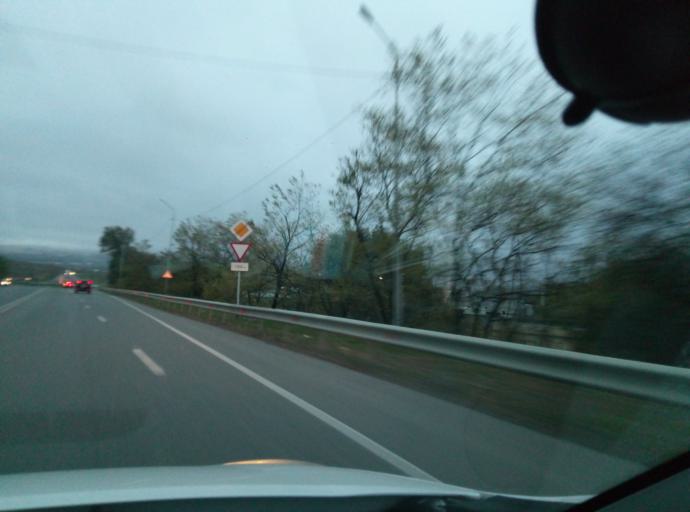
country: RU
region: Stavropol'skiy
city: Vinsady
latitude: 44.0565
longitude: 42.9563
